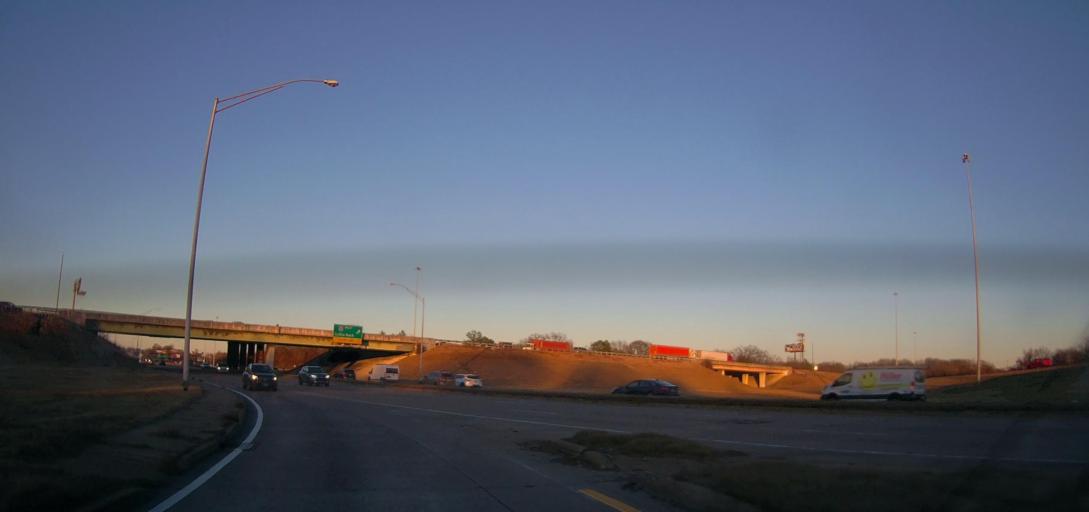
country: US
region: Tennessee
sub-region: Shelby County
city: Bartlett
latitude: 35.1918
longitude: -89.9268
